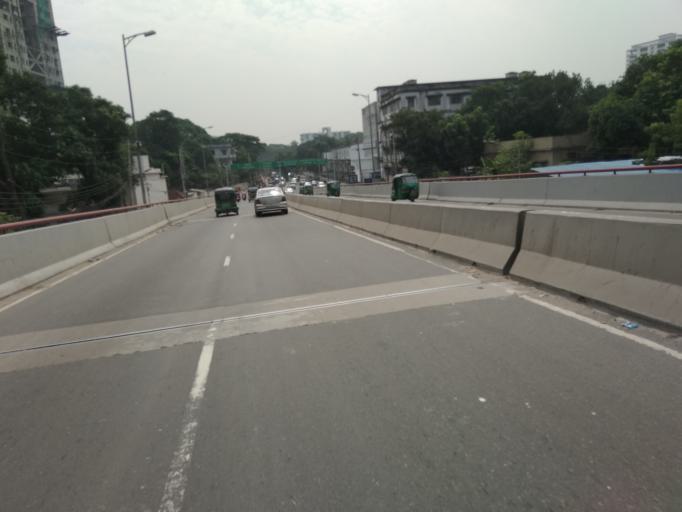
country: BD
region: Dhaka
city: Paltan
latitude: 23.7479
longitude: 90.4039
